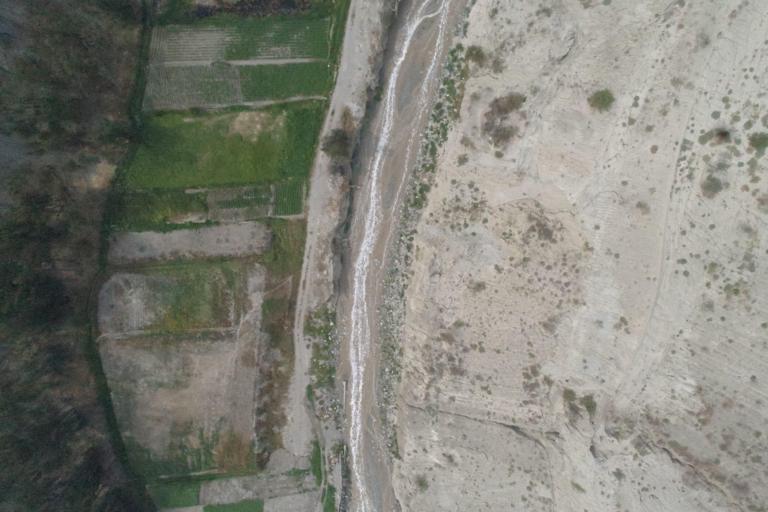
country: BO
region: La Paz
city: La Paz
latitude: -16.5991
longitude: -68.0661
